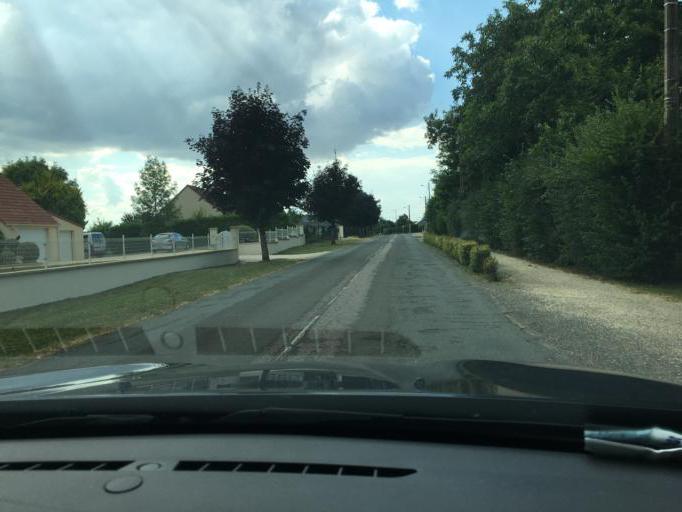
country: FR
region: Centre
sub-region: Departement du Cher
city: Baugy
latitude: 47.0984
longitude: 2.6715
